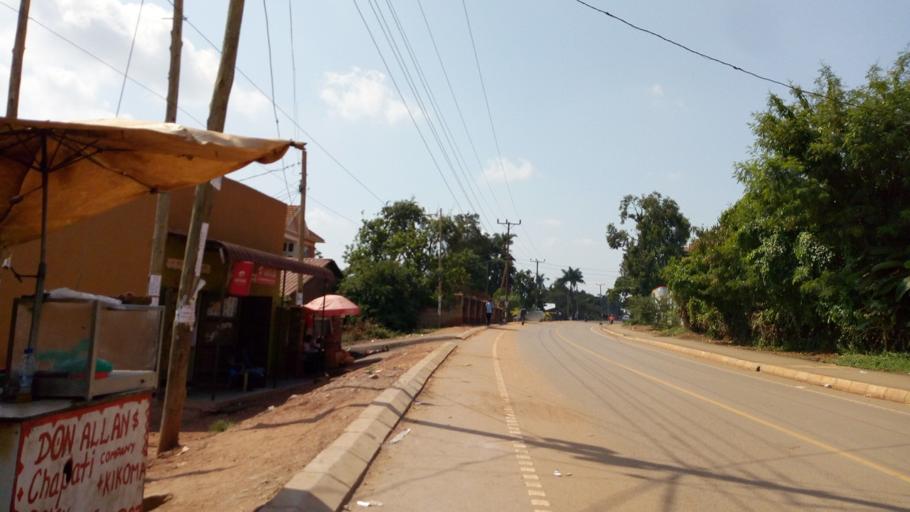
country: UG
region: Central Region
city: Kampala Central Division
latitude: 0.3457
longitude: 32.5641
